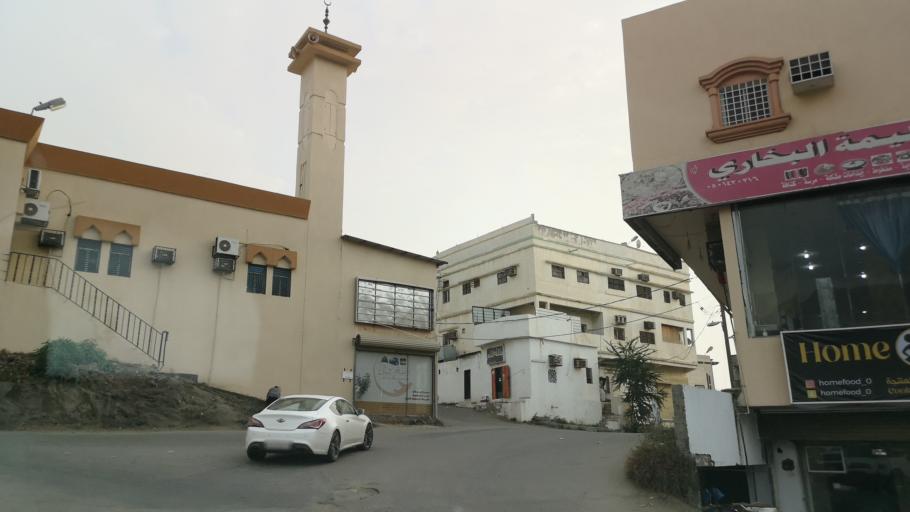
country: YE
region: Sa'dah
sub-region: Monabbih
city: Suq al Khamis
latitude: 17.3370
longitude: 43.1376
